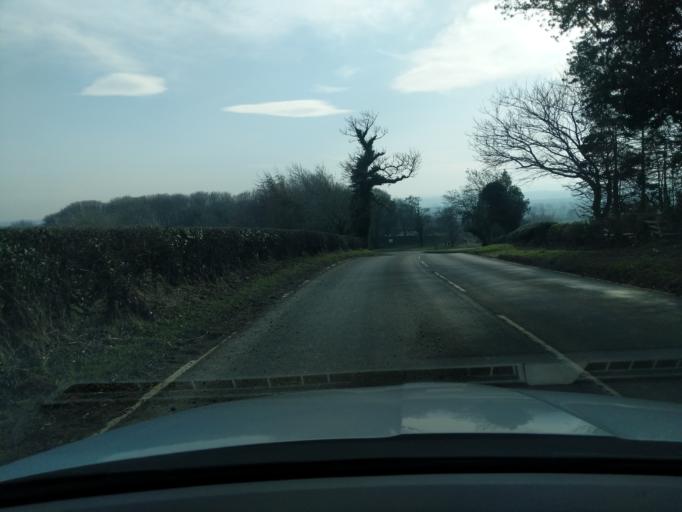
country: GB
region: England
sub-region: North Yorkshire
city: Catterick Garrison
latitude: 54.3427
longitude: -1.6910
